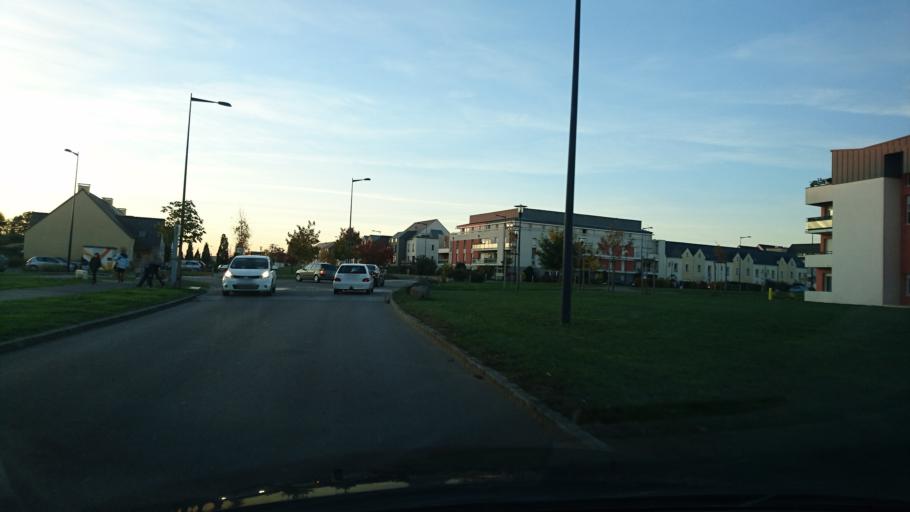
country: FR
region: Brittany
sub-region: Departement d'Ille-et-Vilaine
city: Bruz
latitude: 48.0272
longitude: -1.7572
